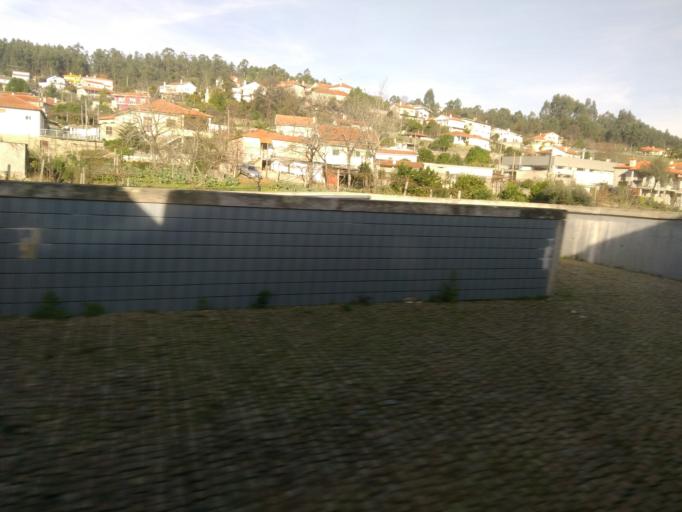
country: PT
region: Braga
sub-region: Braga
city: Oliveira
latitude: 41.4979
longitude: -8.4962
